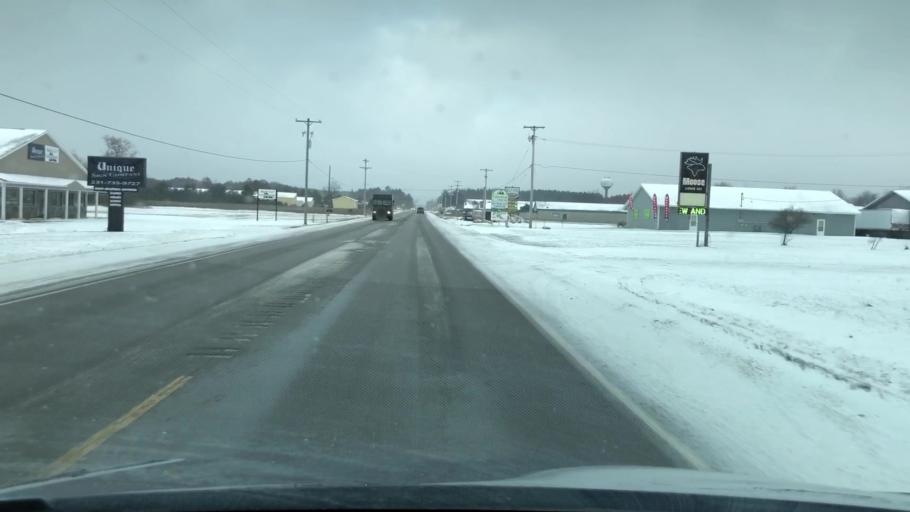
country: US
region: Michigan
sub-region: Wexford County
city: Cadillac
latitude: 44.2813
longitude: -85.4270
